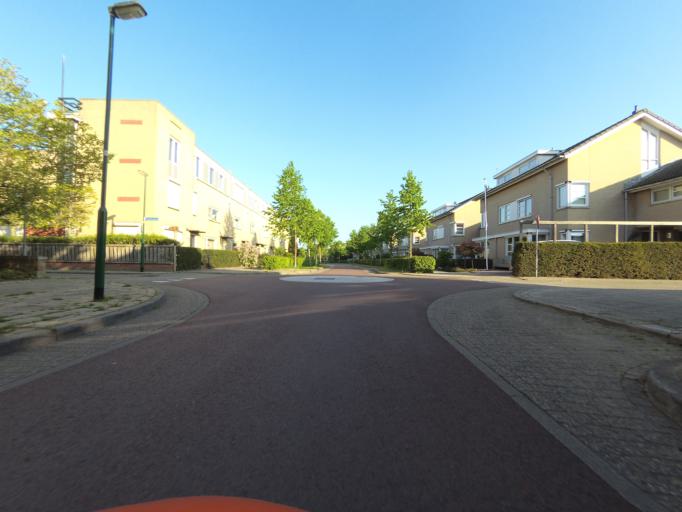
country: NL
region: Utrecht
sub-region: Gemeente Houten
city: Houten
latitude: 52.0232
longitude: 5.1937
